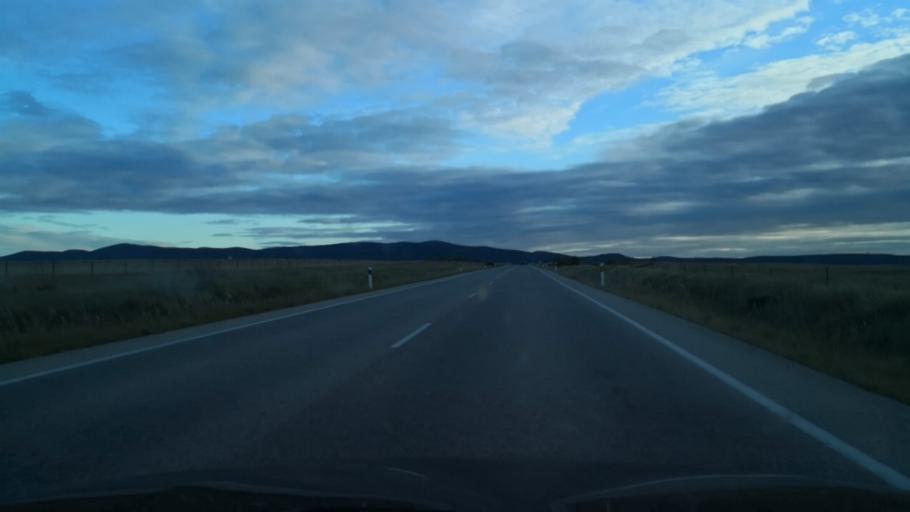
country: ES
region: Extremadura
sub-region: Provincia de Caceres
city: Malpartida de Caceres
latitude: 39.3518
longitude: -6.4689
